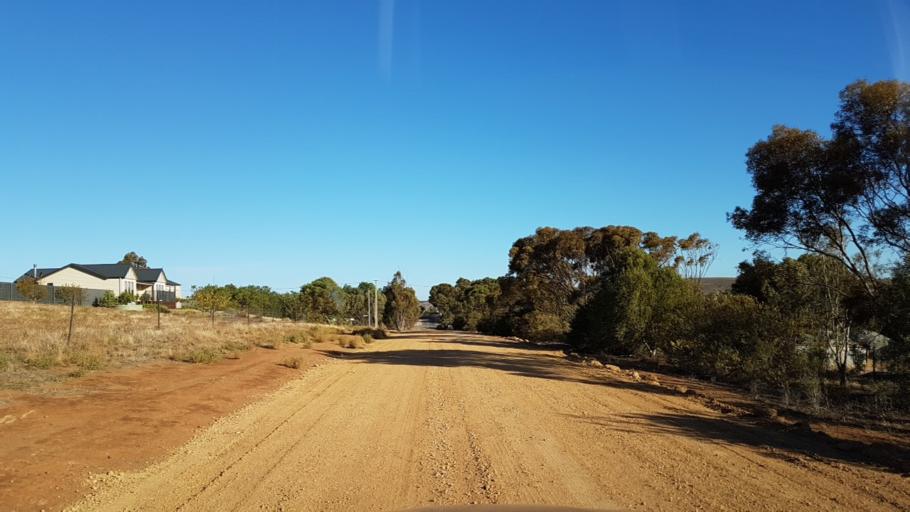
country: AU
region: South Australia
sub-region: Clare and Gilbert Valleys
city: Clare
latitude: -33.6672
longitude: 138.9331
